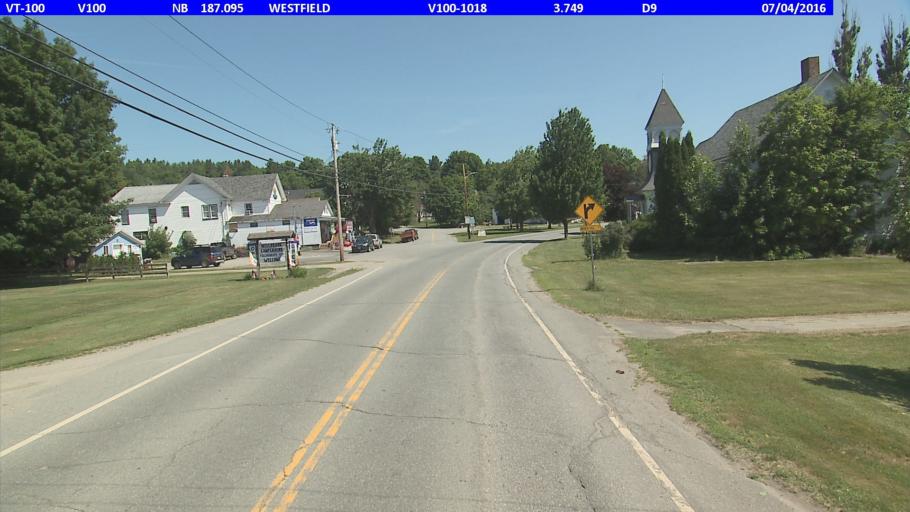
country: US
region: Vermont
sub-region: Orleans County
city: Newport
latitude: 44.8886
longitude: -72.4288
